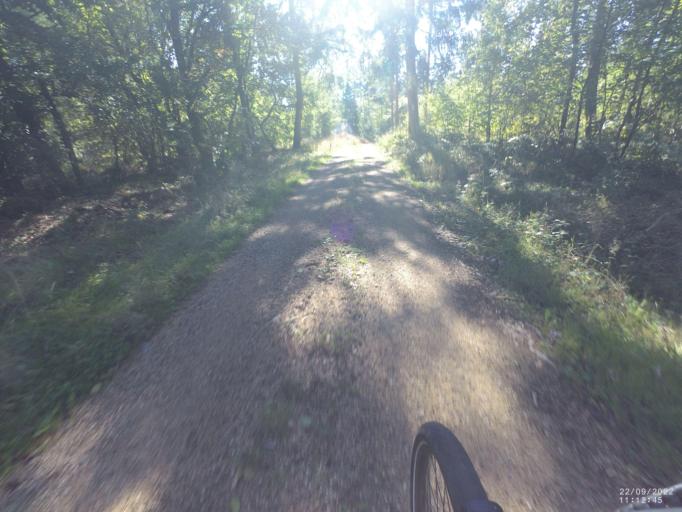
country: DE
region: Rheinland-Pfalz
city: Dockweiler
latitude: 50.2256
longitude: 6.8053
